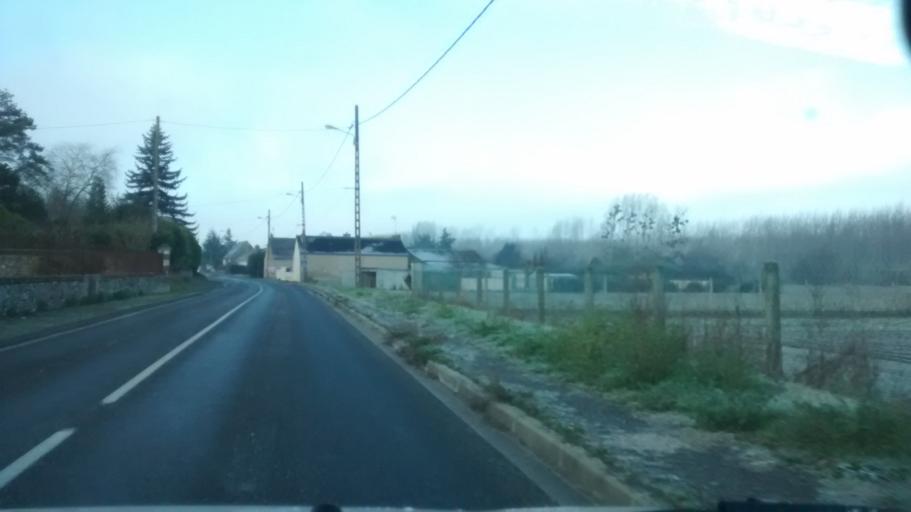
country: FR
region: Centre
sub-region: Departement d'Indre-et-Loire
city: Ballan-Mire
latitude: 47.3589
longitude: 0.6058
